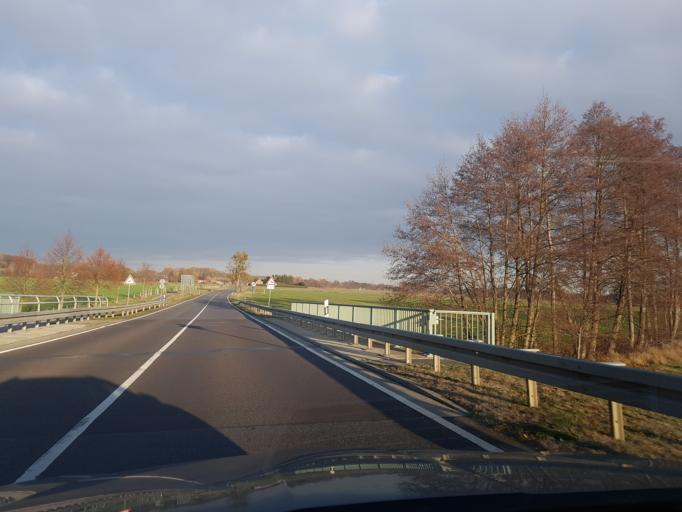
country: DE
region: Brandenburg
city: Luckau
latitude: 51.8658
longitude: 13.7018
